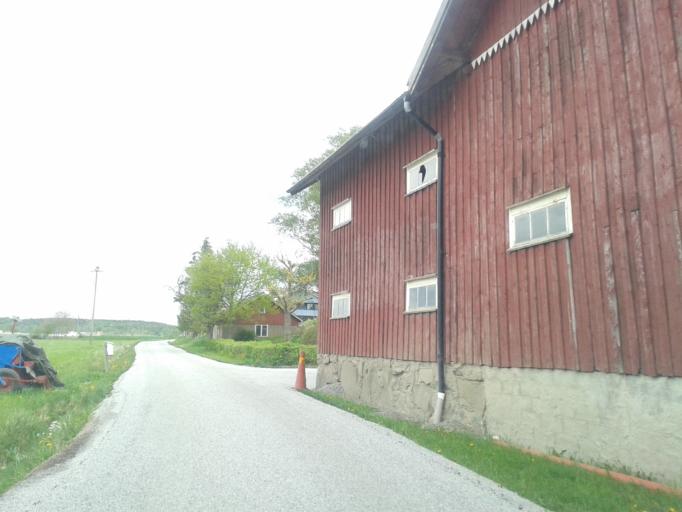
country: SE
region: Vaestra Goetaland
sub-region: Kungalvs Kommun
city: Kungalv
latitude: 57.8975
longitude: 11.9178
